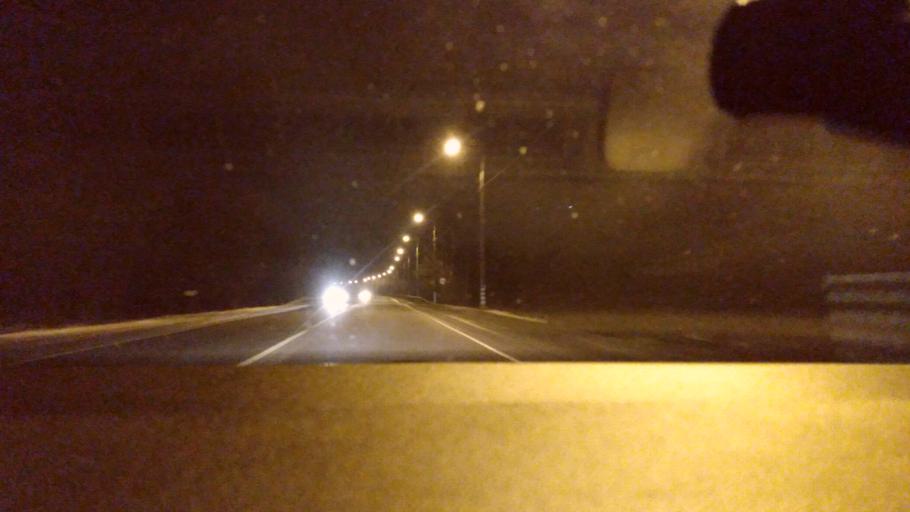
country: RU
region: Moskovskaya
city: Il'inskiy Pogost
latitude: 55.4838
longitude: 38.9265
